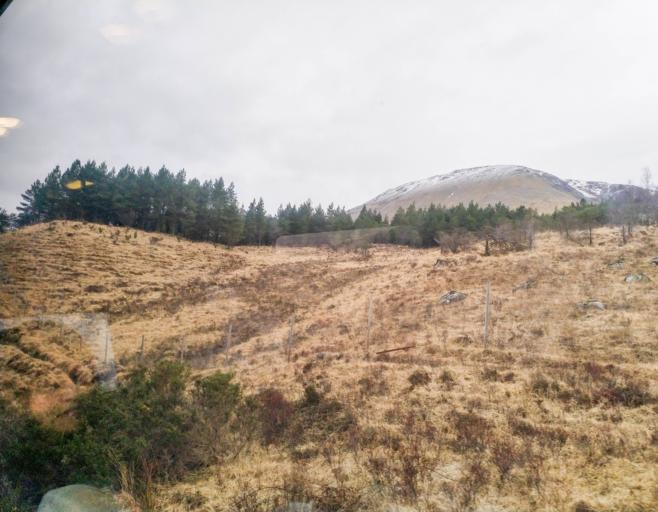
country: GB
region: Scotland
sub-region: Highland
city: Spean Bridge
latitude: 56.5205
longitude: -4.7639
